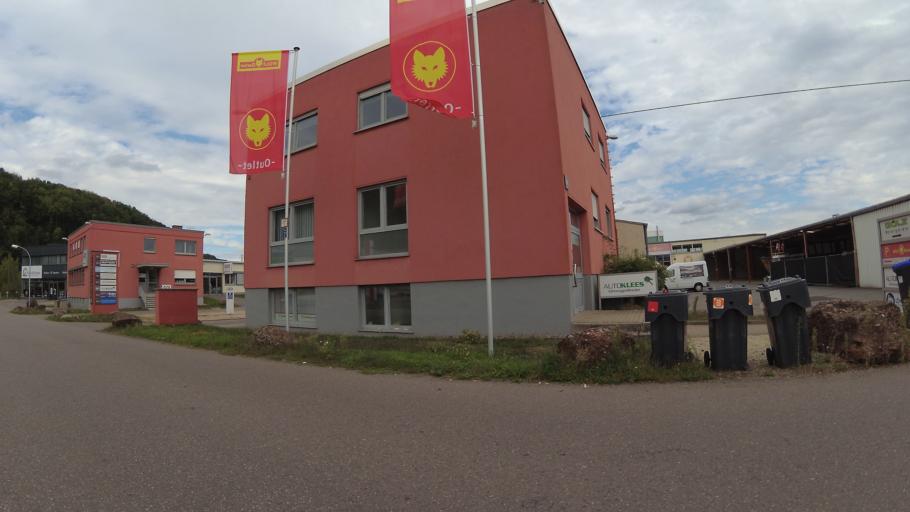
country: FR
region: Lorraine
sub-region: Departement de la Moselle
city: Alsting
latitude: 49.2051
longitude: 7.0217
